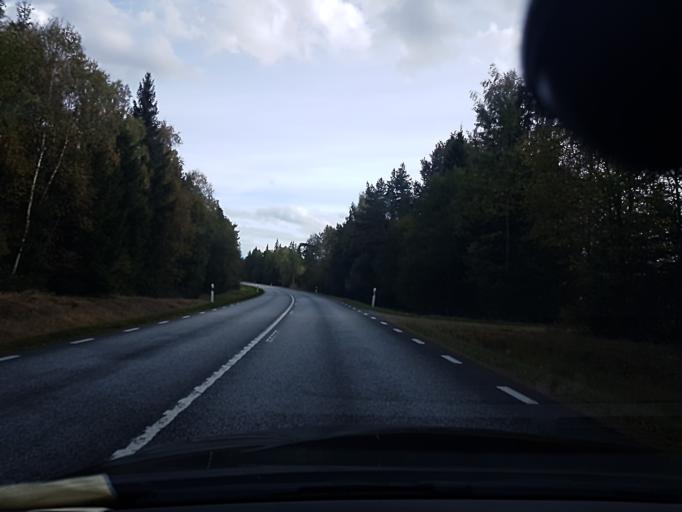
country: SE
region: Joenkoeping
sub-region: Varnamo Kommun
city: Bredaryd
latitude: 57.1885
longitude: 13.7256
